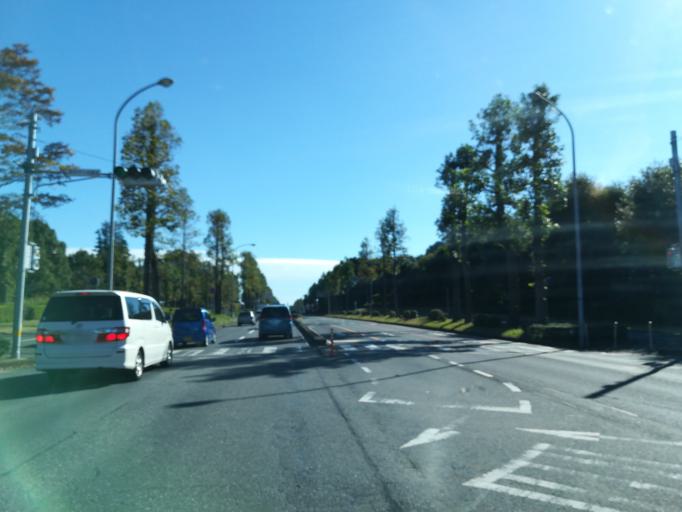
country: JP
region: Ibaraki
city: Naka
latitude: 36.0540
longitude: 140.1216
